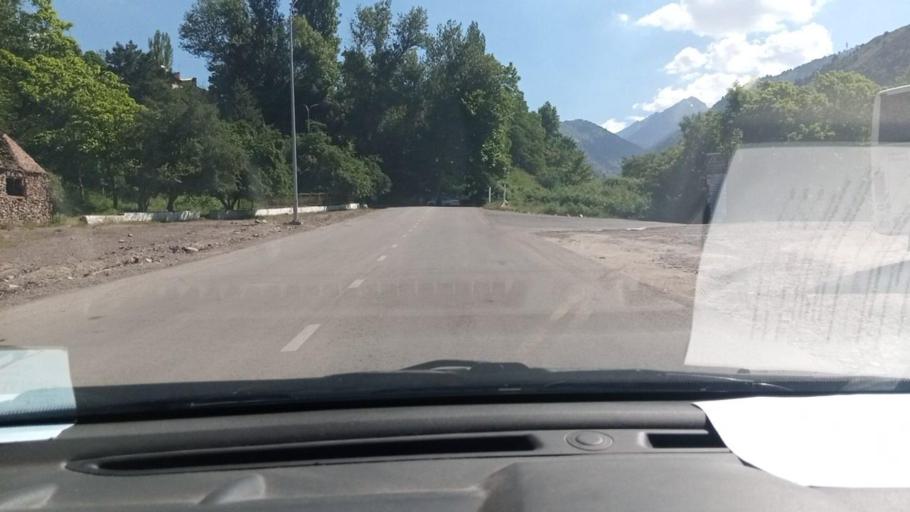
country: UZ
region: Toshkent
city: Yangiobod
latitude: 41.1163
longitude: 70.0914
